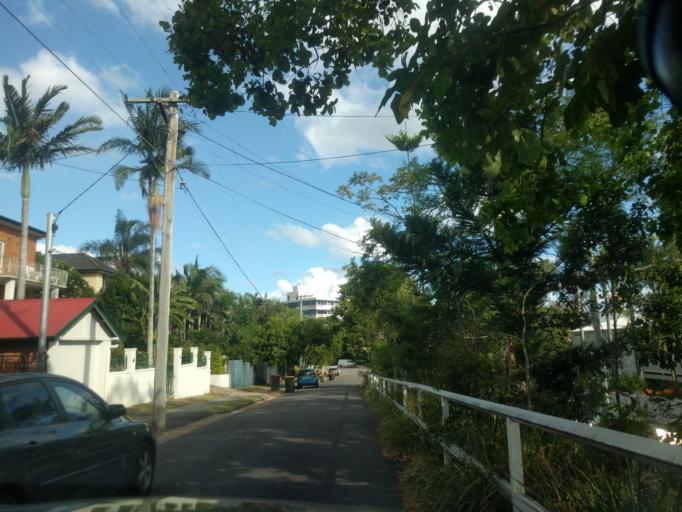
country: AU
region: Queensland
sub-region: Brisbane
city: Woolloongabba
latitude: -27.4740
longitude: 153.0441
